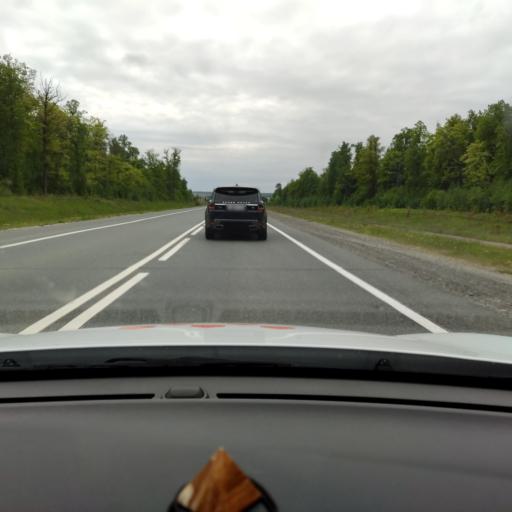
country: RU
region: Tatarstan
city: Pestretsy
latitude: 55.5881
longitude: 49.7152
